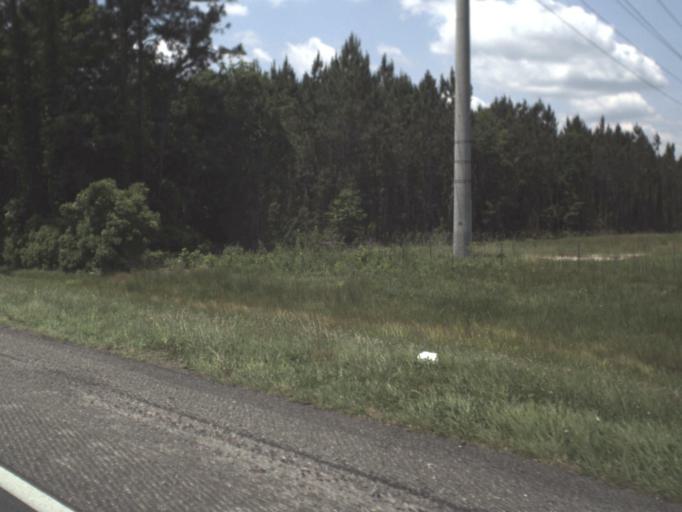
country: US
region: Florida
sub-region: Nassau County
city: Yulee
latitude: 30.4999
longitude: -81.6377
